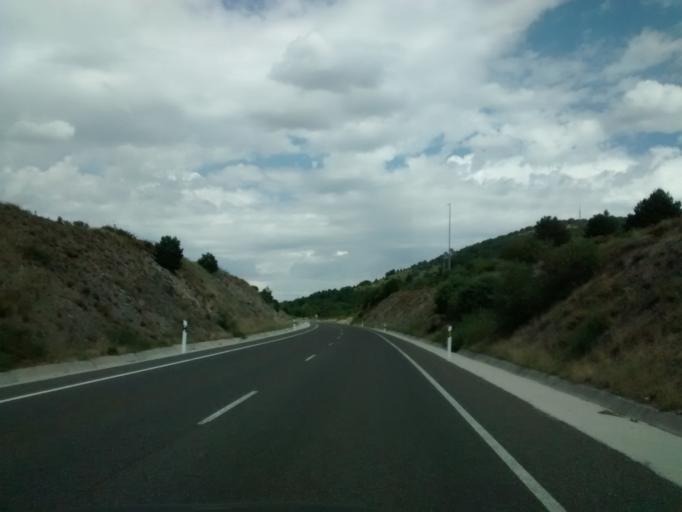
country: ES
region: Castille and Leon
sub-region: Provincia de Segovia
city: Torre Val de San Pedro
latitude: 41.0599
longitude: -3.8759
